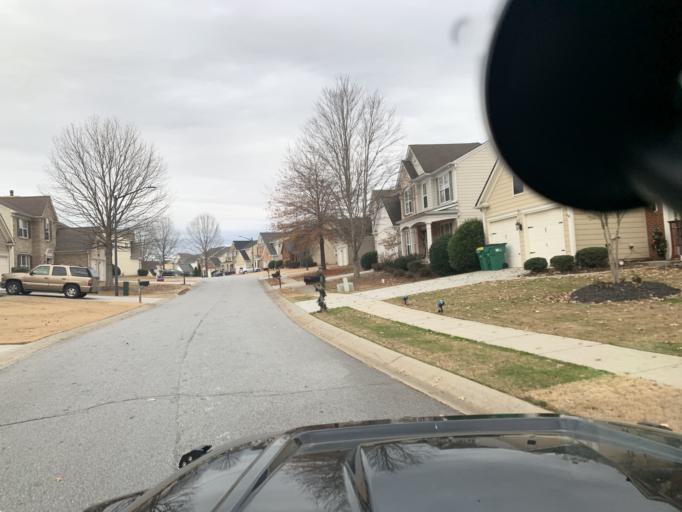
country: US
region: Georgia
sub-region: Cherokee County
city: Woodstock
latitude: 34.0957
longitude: -84.4604
